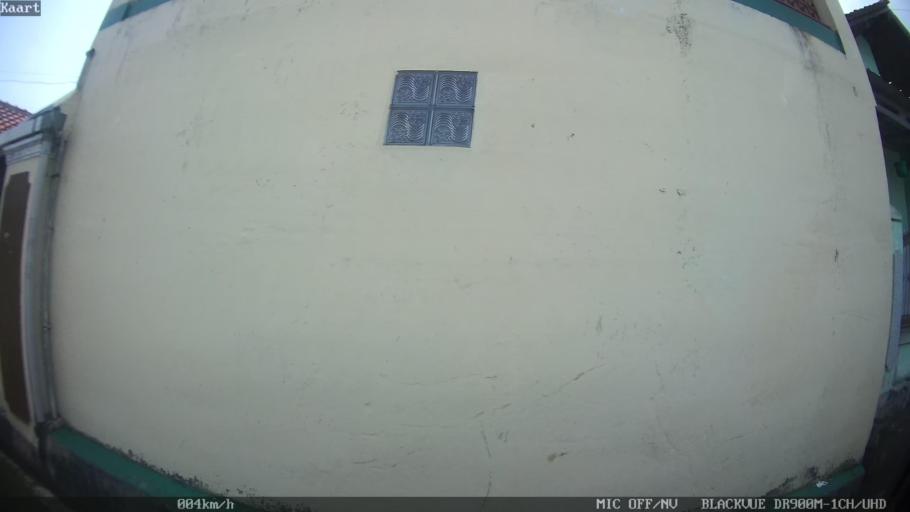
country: ID
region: Lampung
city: Bandarlampung
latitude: -5.4366
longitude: 105.2667
